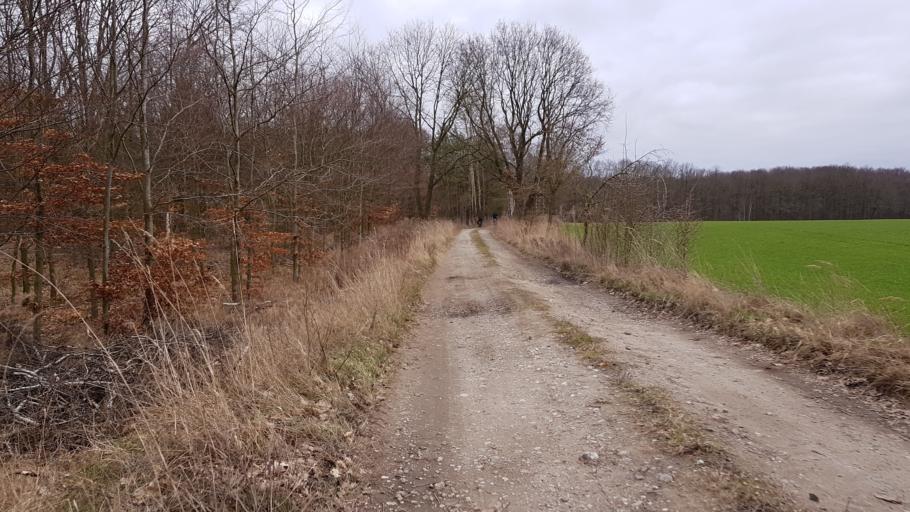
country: PL
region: West Pomeranian Voivodeship
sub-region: Powiat gryfinski
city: Banie
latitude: 53.0740
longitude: 14.7307
